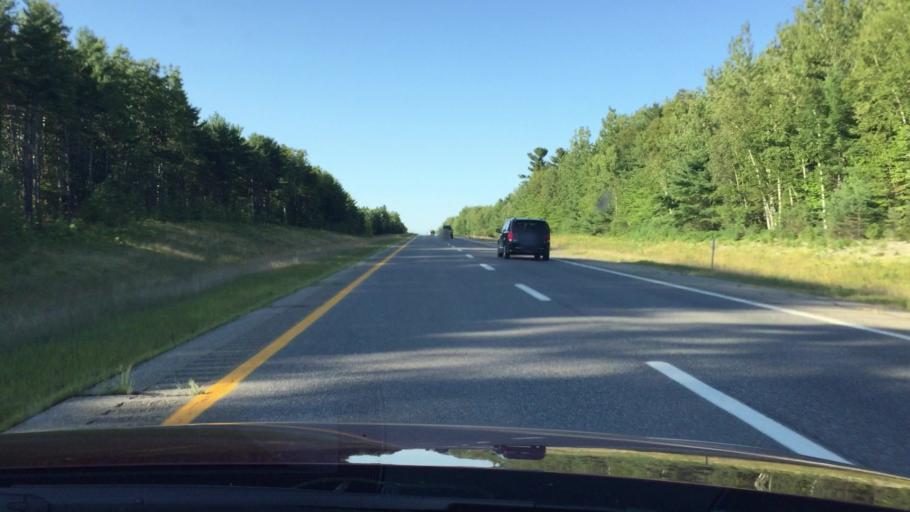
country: US
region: Maine
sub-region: Penobscot County
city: Lincoln
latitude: 45.4082
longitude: -68.5953
